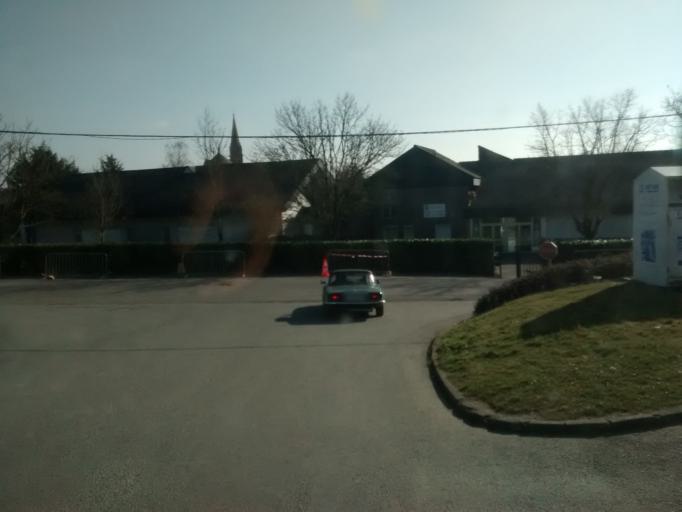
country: FR
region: Brittany
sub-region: Departement d'Ille-et-Vilaine
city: Maure-de-Bretagne
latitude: 47.8944
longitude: -1.9898
